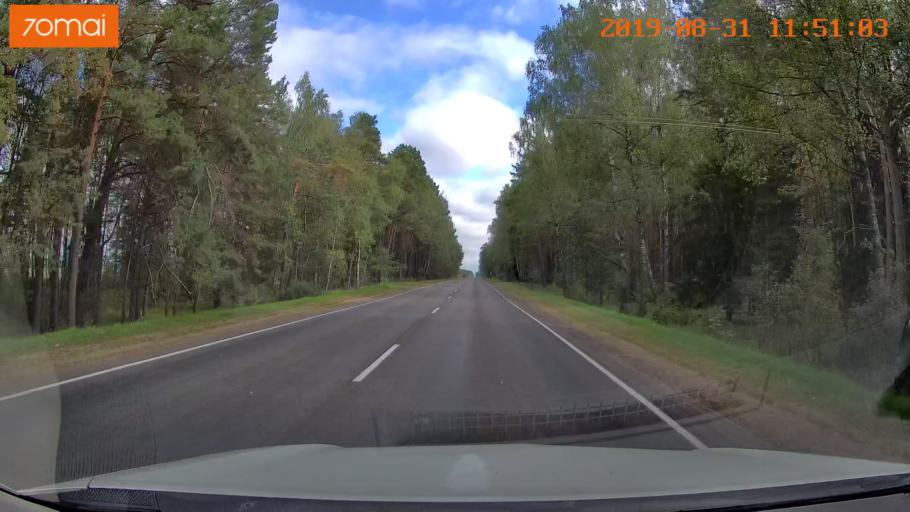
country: BY
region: Mogilev
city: Cherykaw
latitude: 53.6122
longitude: 31.4966
